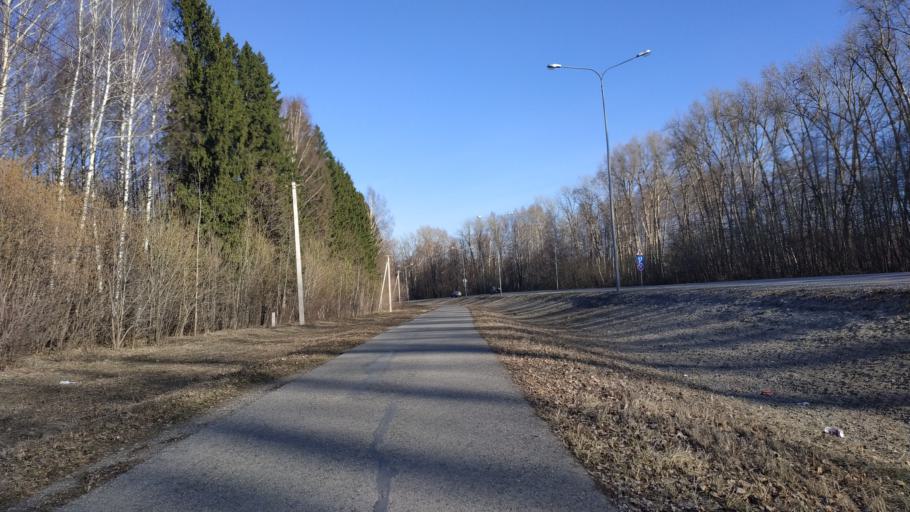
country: RU
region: Chuvashia
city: Novyye Lapsary
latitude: 56.1288
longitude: 47.1187
